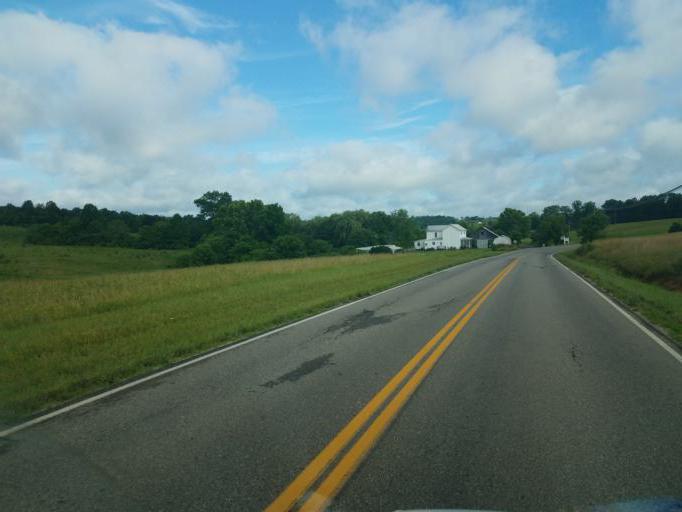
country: US
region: Ohio
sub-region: Jackson County
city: Oak Hill
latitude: 38.7989
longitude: -82.4003
